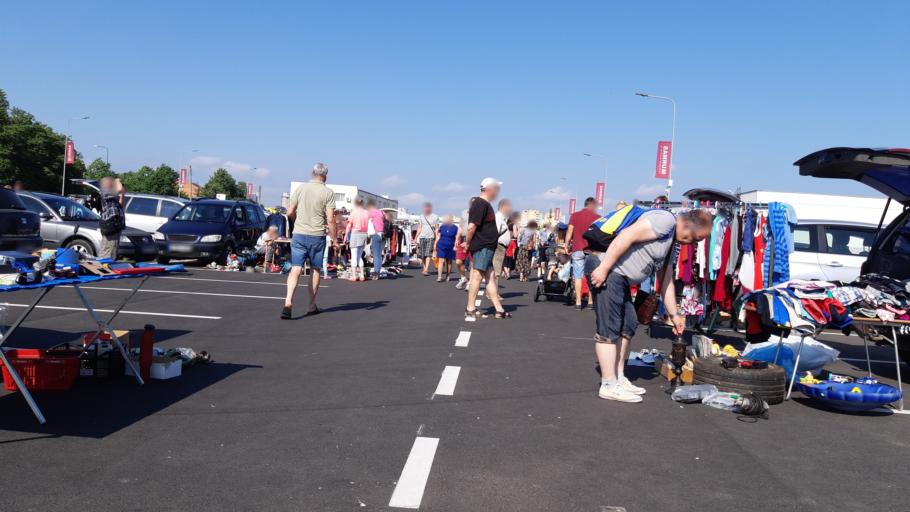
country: LT
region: Kauno apskritis
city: Dainava (Kaunas)
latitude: 54.9139
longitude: 23.9967
